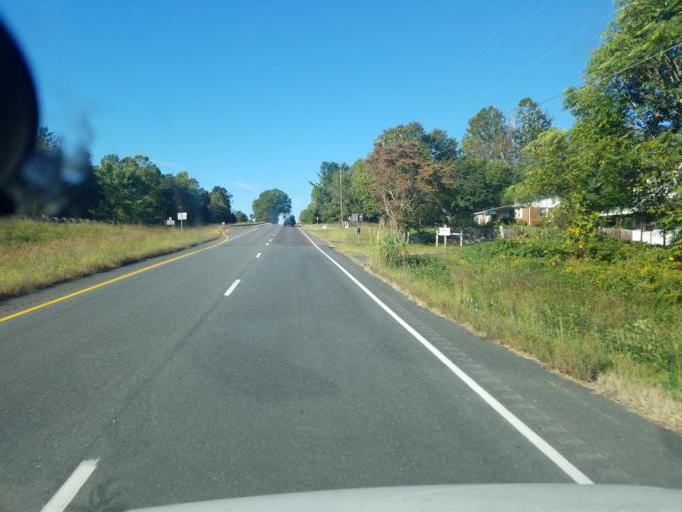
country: US
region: Virginia
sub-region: Madison County
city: Brightwood
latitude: 38.4320
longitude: -78.1632
